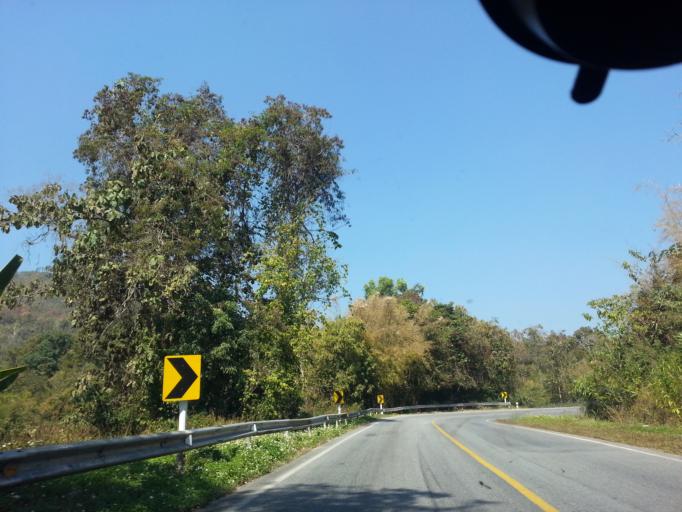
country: TH
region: Chiang Mai
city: Chai Prakan
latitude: 19.5696
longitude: 99.0786
